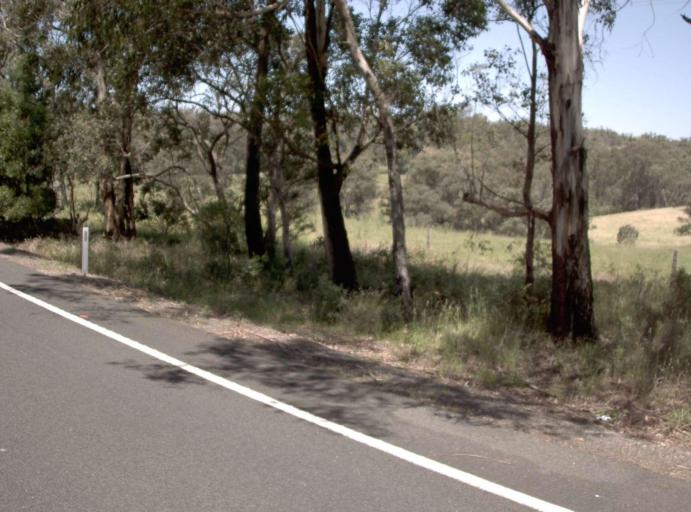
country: AU
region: Victoria
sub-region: East Gippsland
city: Lakes Entrance
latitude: -37.7473
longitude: 148.1761
